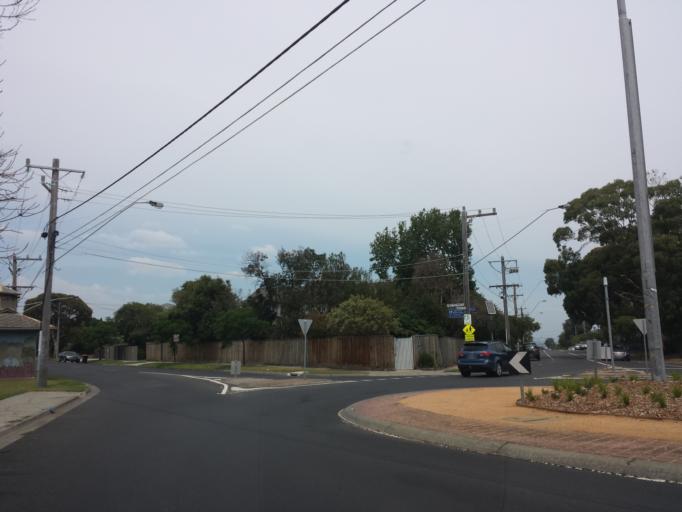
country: AU
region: Victoria
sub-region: Kingston
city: Mentone
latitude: -37.9880
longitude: 145.0703
